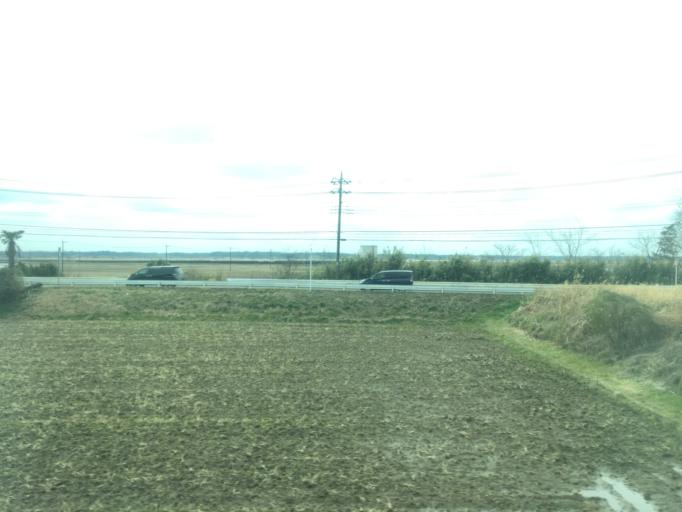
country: JP
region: Chiba
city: Narita
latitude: 35.8111
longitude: 140.2730
